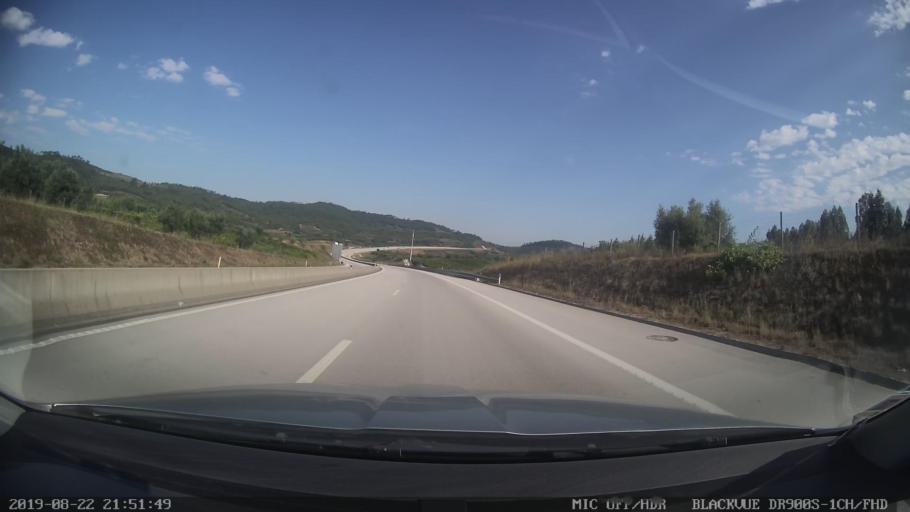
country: PT
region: Coimbra
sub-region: Miranda do Corvo
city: Miranda do Corvo
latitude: 40.0878
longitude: -8.3859
